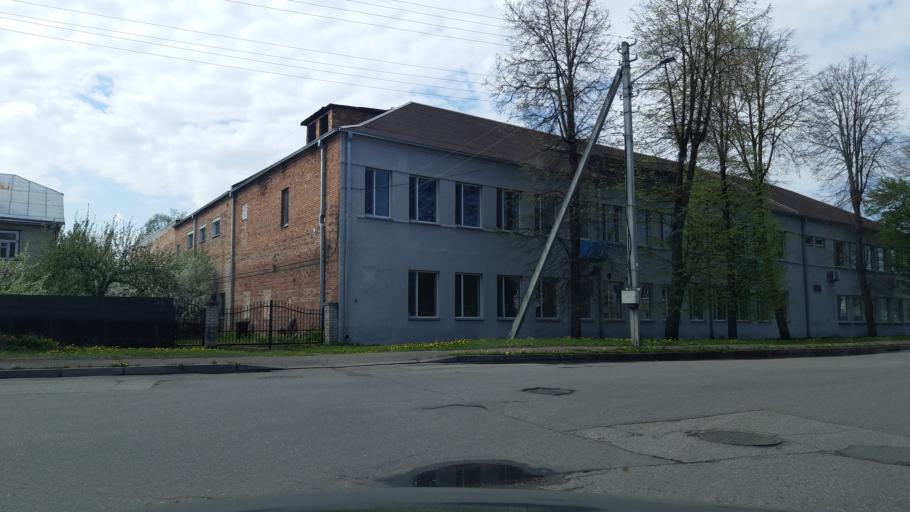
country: LT
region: Kauno apskritis
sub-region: Kaunas
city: Silainiai
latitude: 54.9091
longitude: 23.8779
